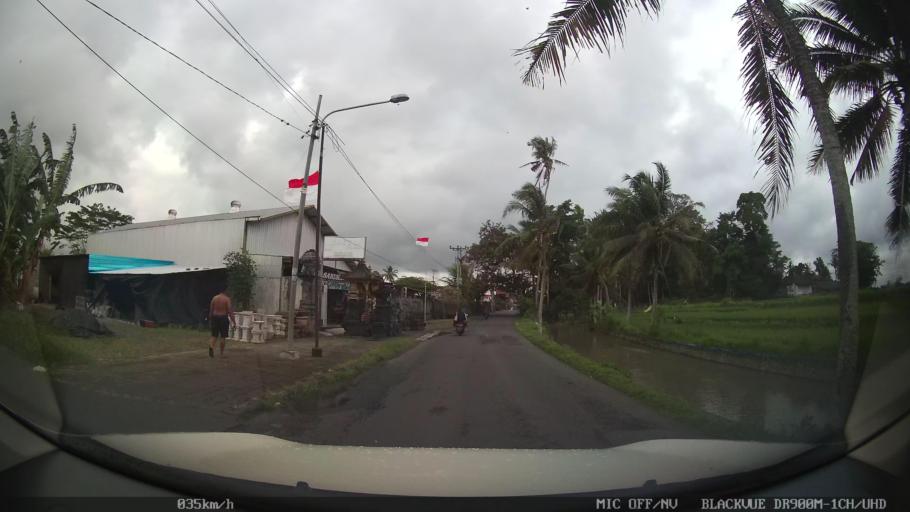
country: ID
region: Bali
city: Banjar Cemenggon
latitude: -8.5511
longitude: 115.1938
